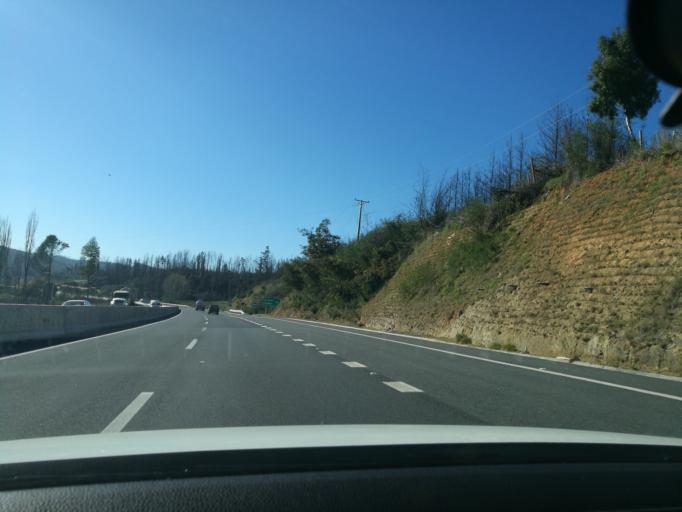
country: CL
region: Biobio
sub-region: Provincia de Concepcion
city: Chiguayante
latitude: -36.8569
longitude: -72.8864
